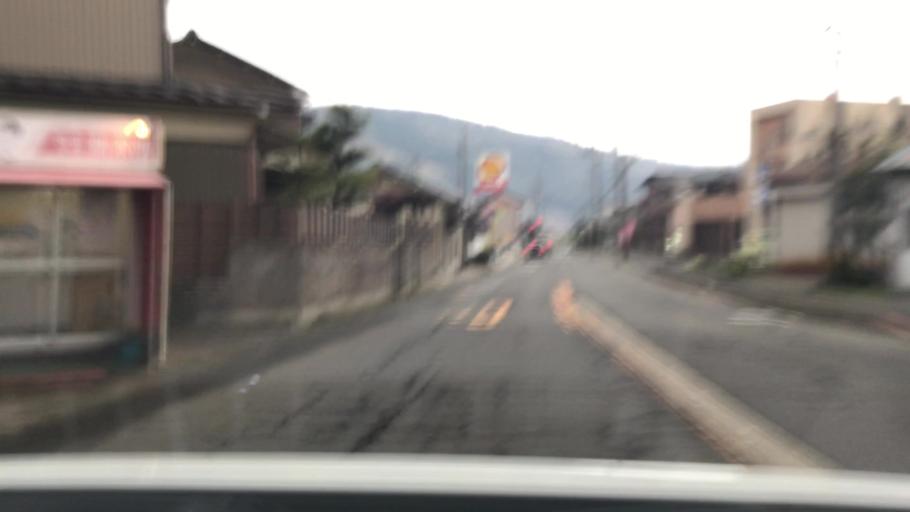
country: JP
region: Fukui
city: Fukui-shi
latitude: 36.0856
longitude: 136.1903
